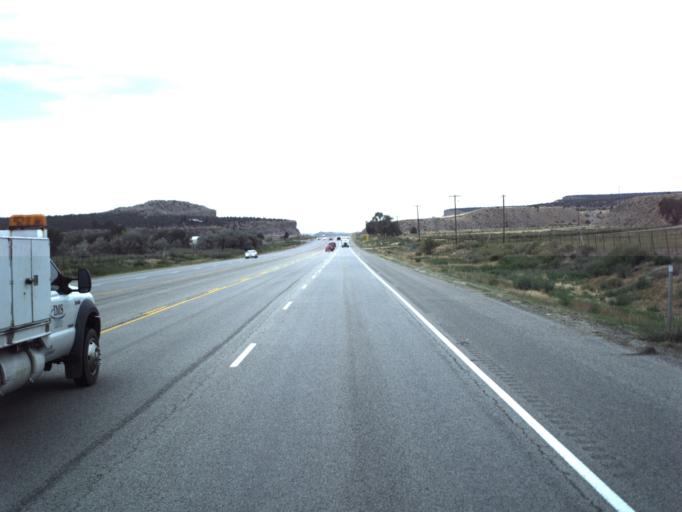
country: US
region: Utah
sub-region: Carbon County
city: Spring Glen
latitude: 39.6600
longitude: -110.8609
